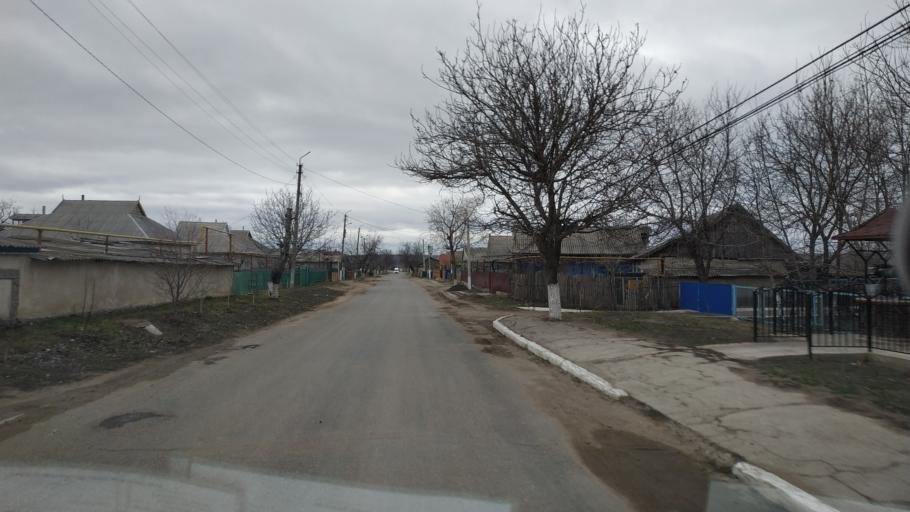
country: MD
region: Causeni
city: Causeni
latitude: 46.6640
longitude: 29.4876
